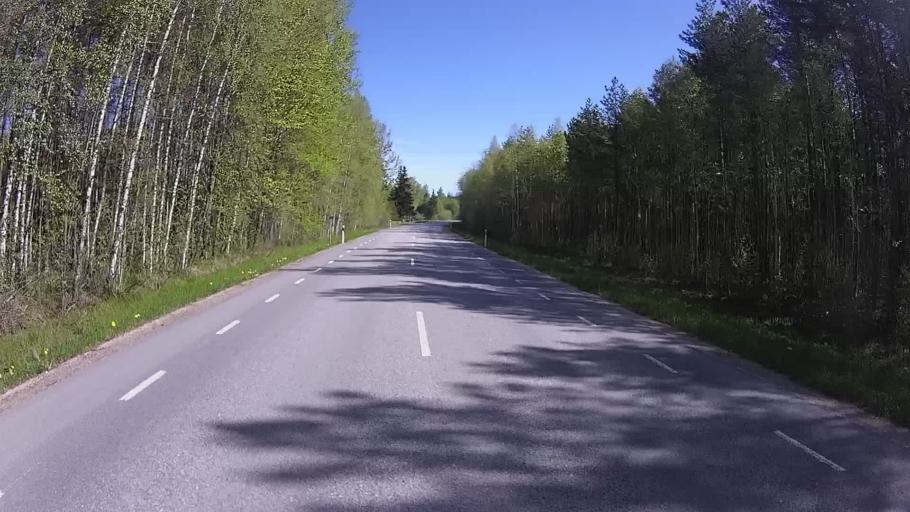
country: EE
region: Polvamaa
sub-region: Raepina vald
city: Rapina
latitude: 58.0256
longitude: 27.5580
